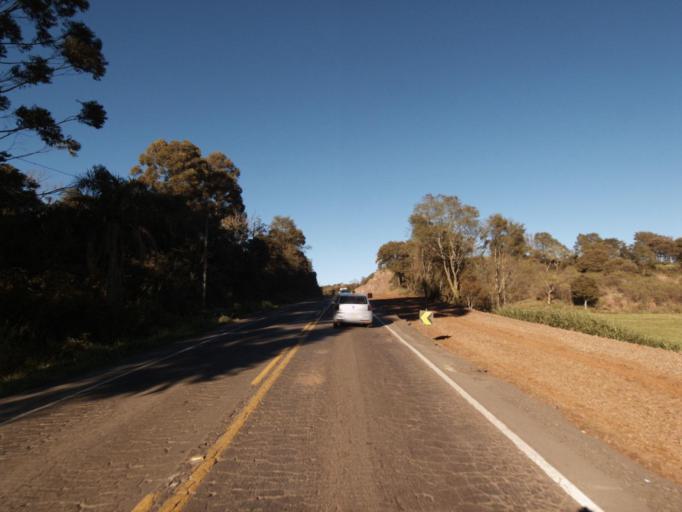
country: AR
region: Misiones
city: Bernardo de Irigoyen
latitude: -26.6315
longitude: -53.5180
